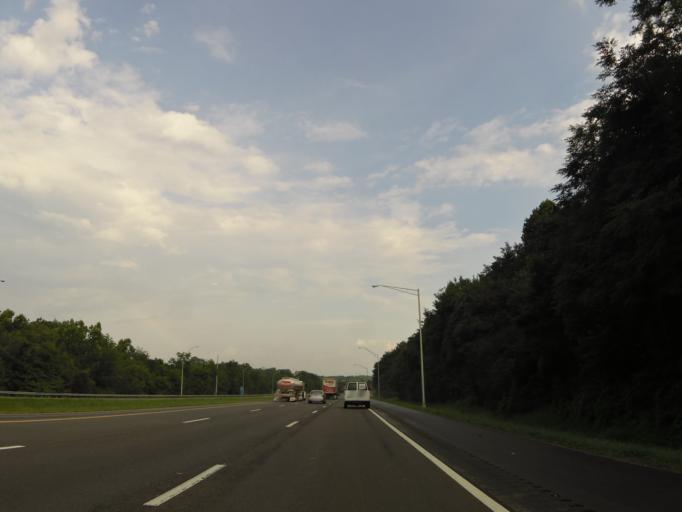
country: US
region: Tennessee
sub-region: Knox County
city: Knoxville
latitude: 36.0270
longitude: -83.8640
